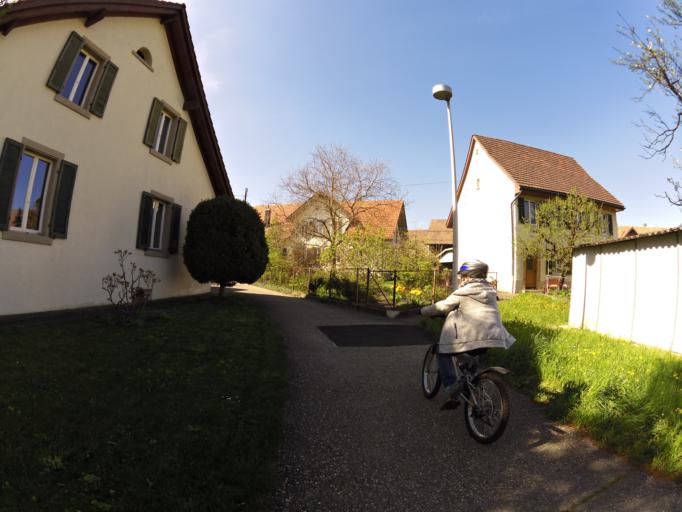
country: CH
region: Solothurn
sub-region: Bezirk Goesgen
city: Niedererlinsbach
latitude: 47.3978
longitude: 8.0070
